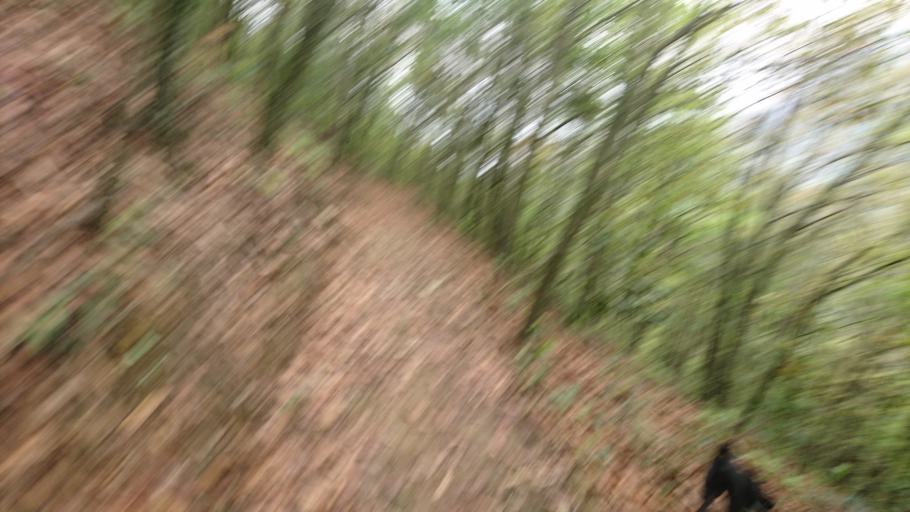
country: MX
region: Nuevo Leon
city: Garza Garcia
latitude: 25.6030
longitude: -100.3364
